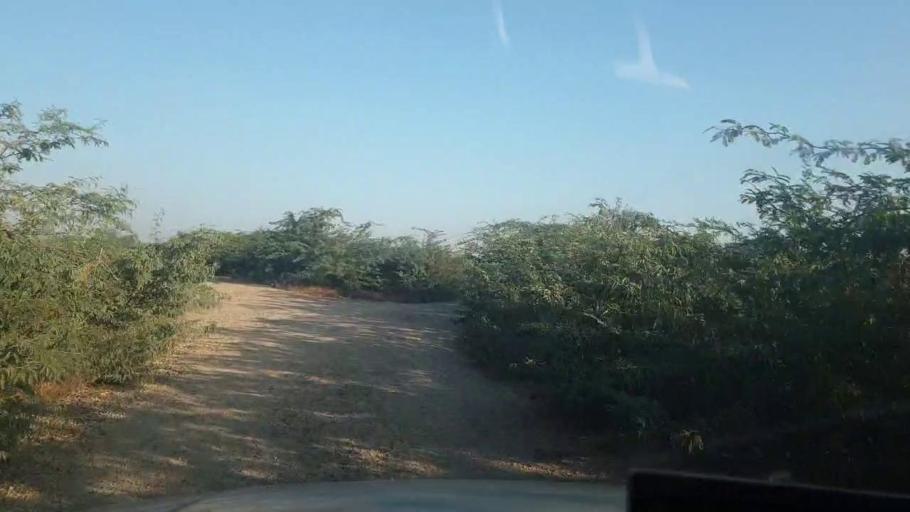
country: PK
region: Sindh
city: Thatta
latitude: 24.7116
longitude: 67.8467
